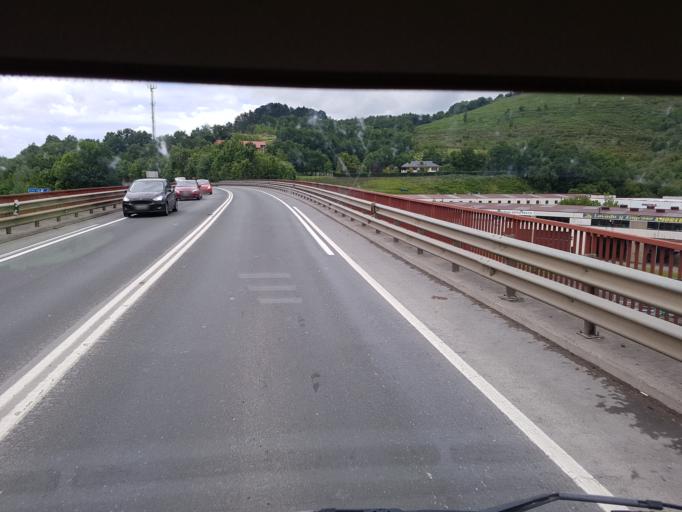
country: ES
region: Basque Country
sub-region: Bizkaia
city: Amorebieta
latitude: 43.2121
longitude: -2.7217
